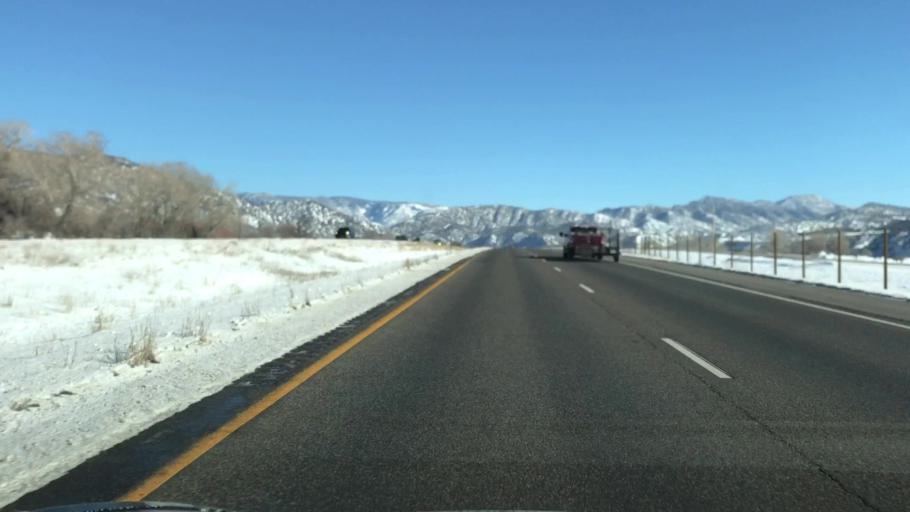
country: US
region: Colorado
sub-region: Garfield County
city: New Castle
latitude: 39.5520
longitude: -107.5900
